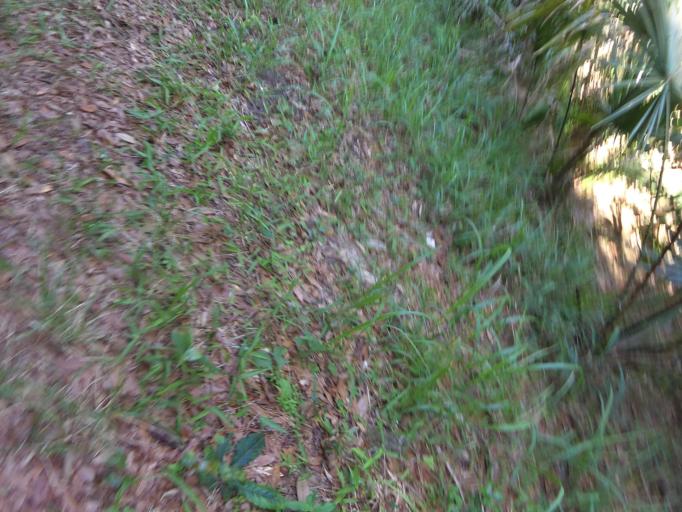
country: US
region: Florida
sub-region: Duval County
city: Atlantic Beach
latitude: 30.4402
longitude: -81.4699
